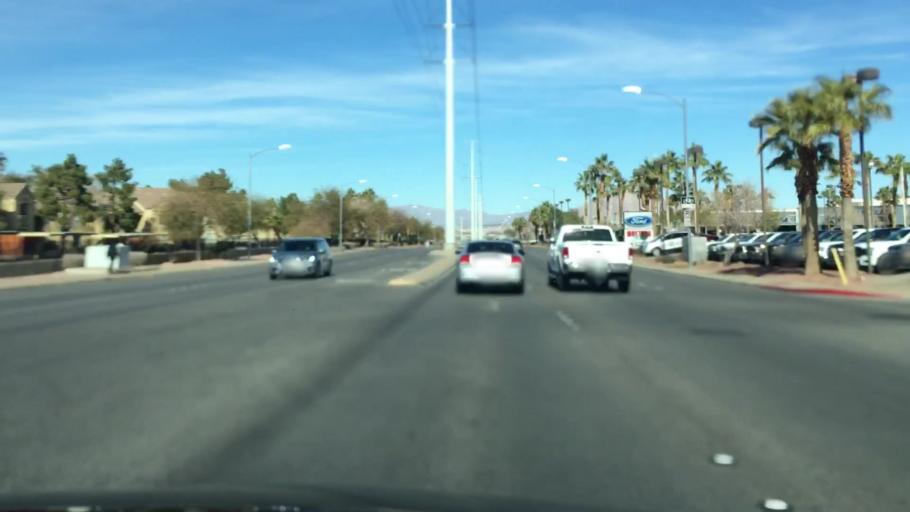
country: US
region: Nevada
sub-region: Clark County
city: Henderson
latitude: 36.0488
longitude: -115.0290
